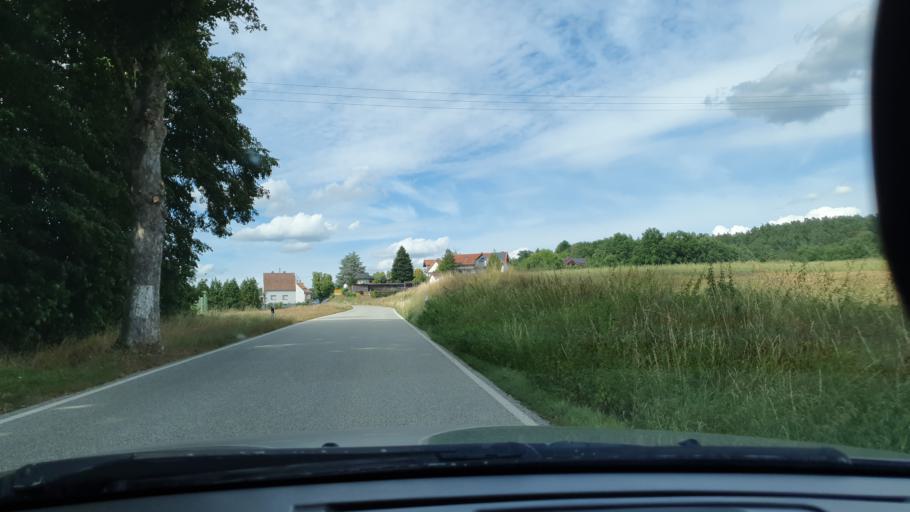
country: DE
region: Rheinland-Pfalz
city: Steinalben
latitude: 49.3226
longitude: 7.6510
